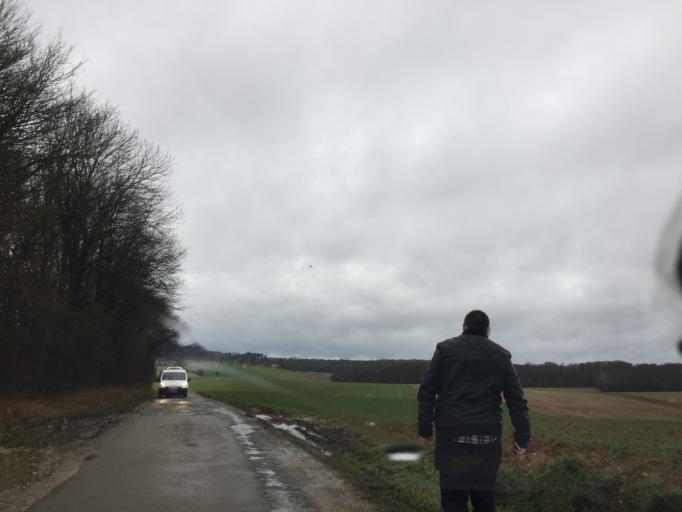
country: FR
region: Franche-Comte
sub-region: Departement du Jura
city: Orchamps
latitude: 47.1974
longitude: 5.6435
